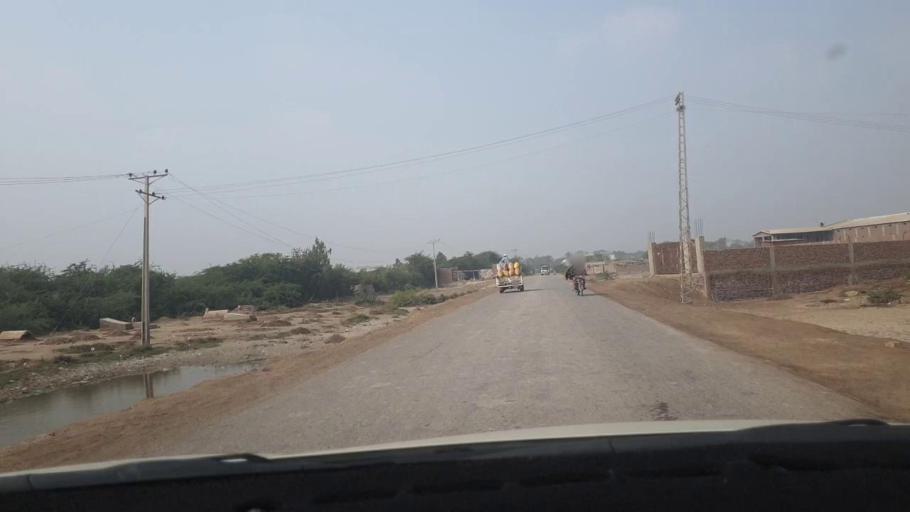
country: PK
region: Sindh
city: Tando Muhammad Khan
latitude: 25.1118
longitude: 68.5353
